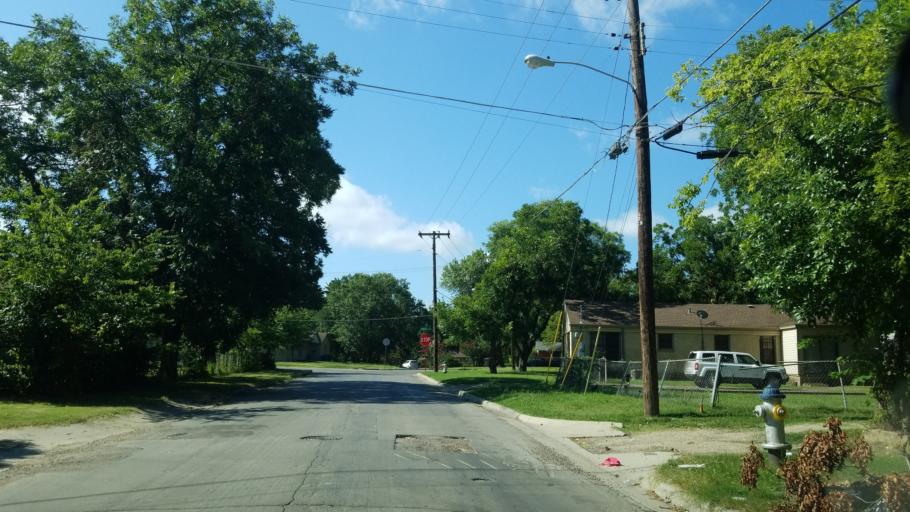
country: US
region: Texas
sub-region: Dallas County
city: Dallas
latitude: 32.7176
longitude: -96.7999
